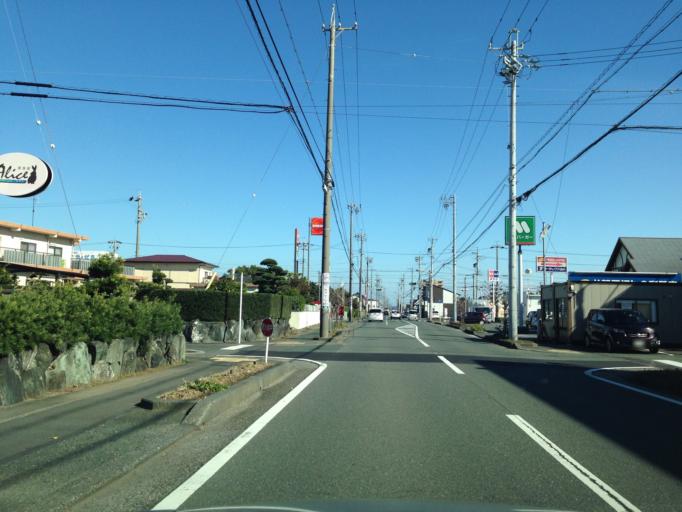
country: JP
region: Shizuoka
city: Fukuroi
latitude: 34.7514
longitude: 137.9135
